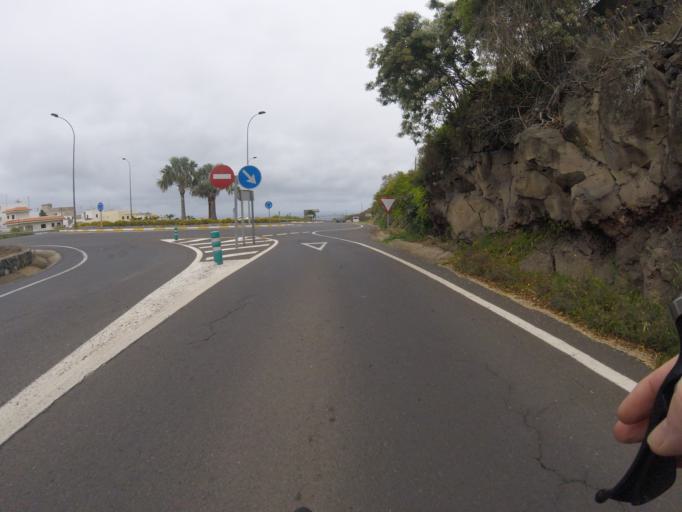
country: ES
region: Canary Islands
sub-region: Provincia de Santa Cruz de Tenerife
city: Tegueste
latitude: 28.5365
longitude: -16.3587
